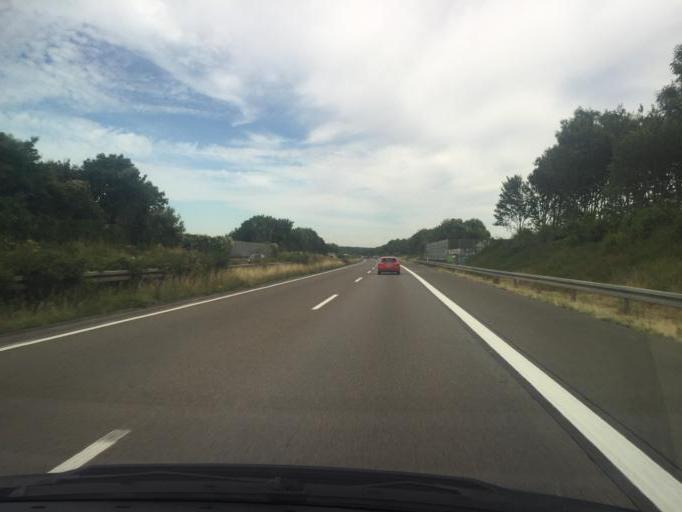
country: DE
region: North Rhine-Westphalia
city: Rheinberg
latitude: 51.5504
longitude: 6.5522
